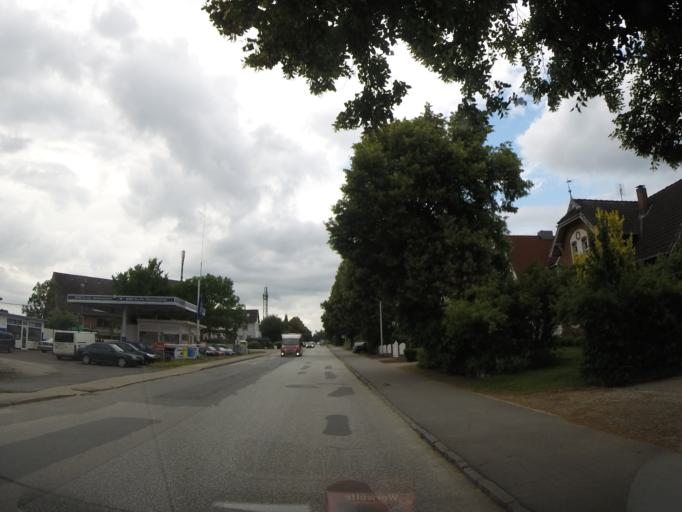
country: DE
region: Schleswig-Holstein
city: Ratekau
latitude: 53.9856
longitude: 10.7123
